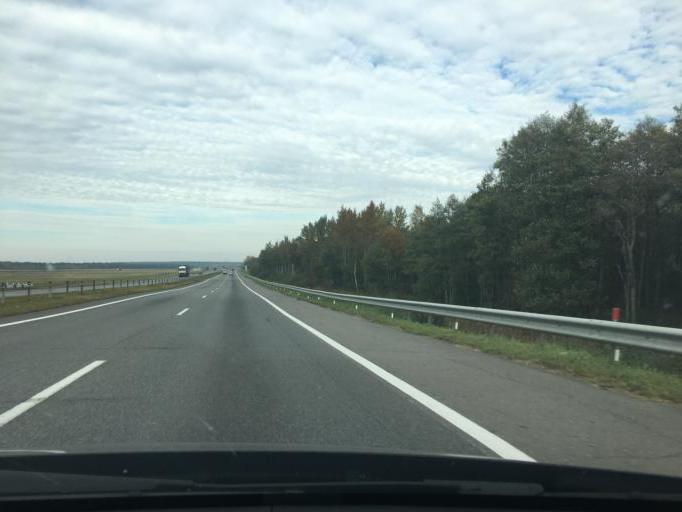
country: BY
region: Minsk
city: Enyerhyetykaw
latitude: 53.6013
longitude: 27.0448
